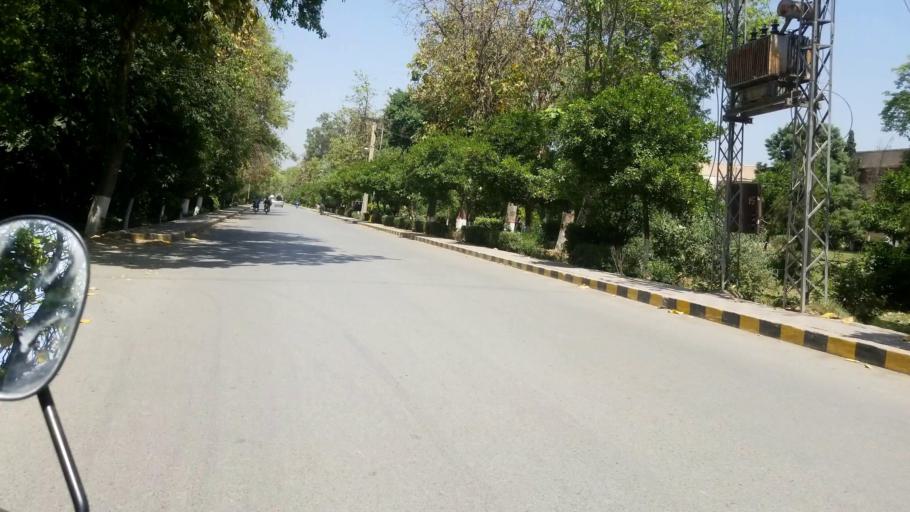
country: PK
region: Khyber Pakhtunkhwa
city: Peshawar
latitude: 34.0033
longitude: 71.4864
